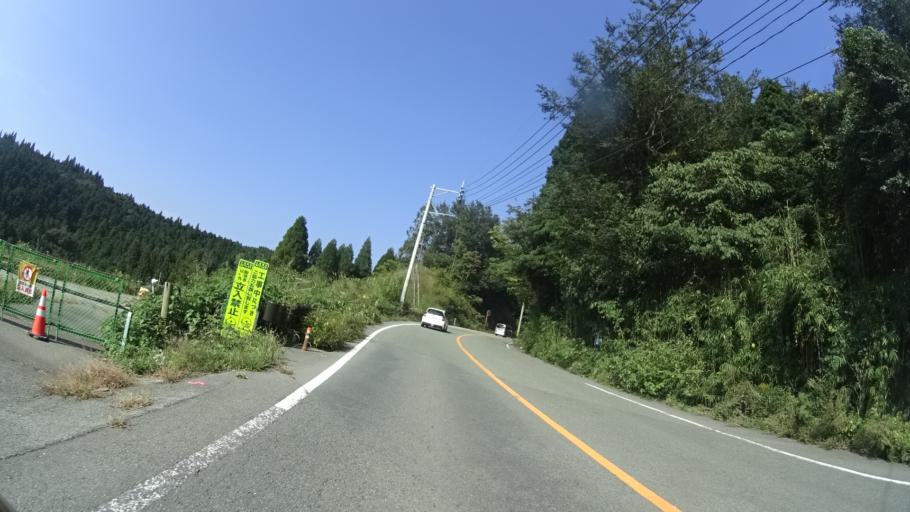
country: JP
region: Kumamoto
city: Ozu
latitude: 32.9007
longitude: 130.9391
